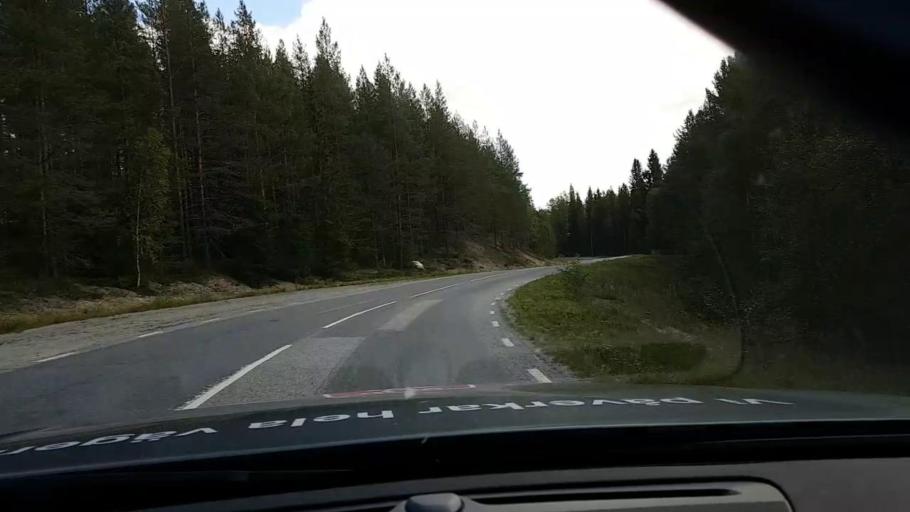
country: SE
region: Vaesterbotten
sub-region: Asele Kommun
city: Asele
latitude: 63.7961
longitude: 17.5653
